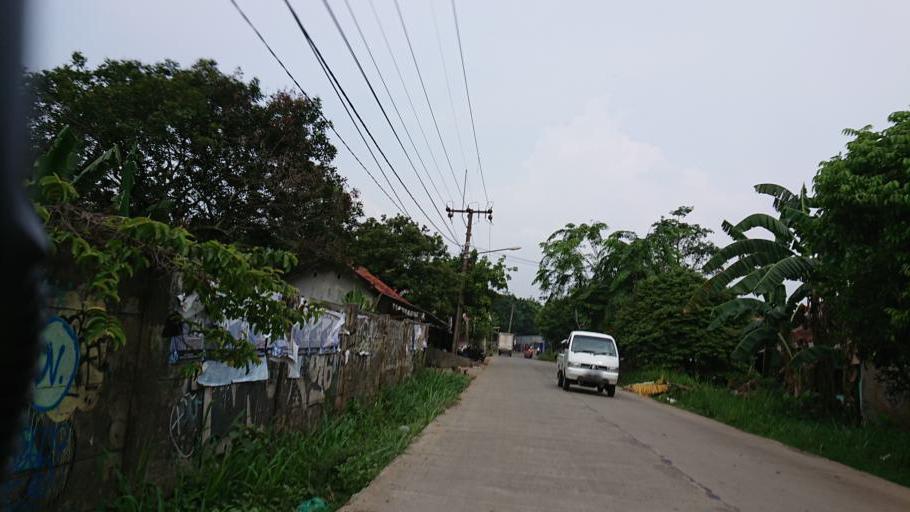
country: ID
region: West Java
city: Parung
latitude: -6.4529
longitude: 106.7016
